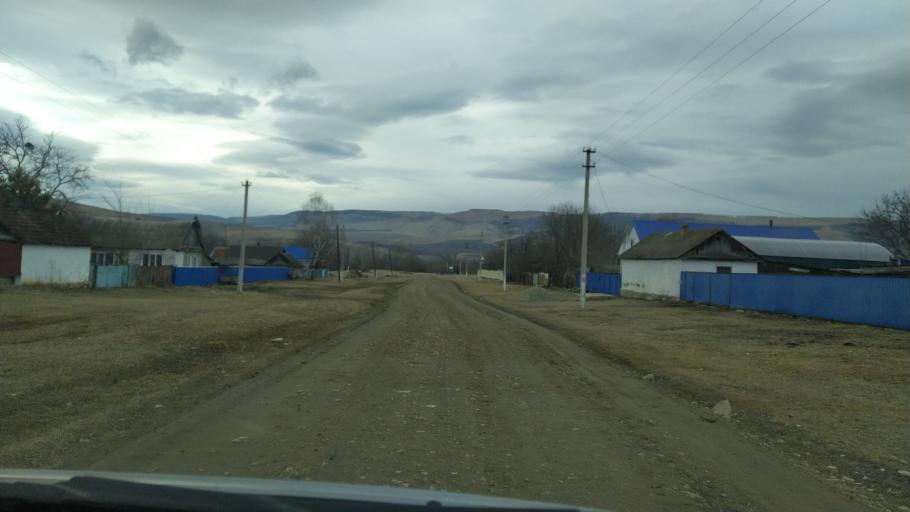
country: RU
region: Krasnodarskiy
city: Peredovaya
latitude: 44.0837
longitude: 41.3667
